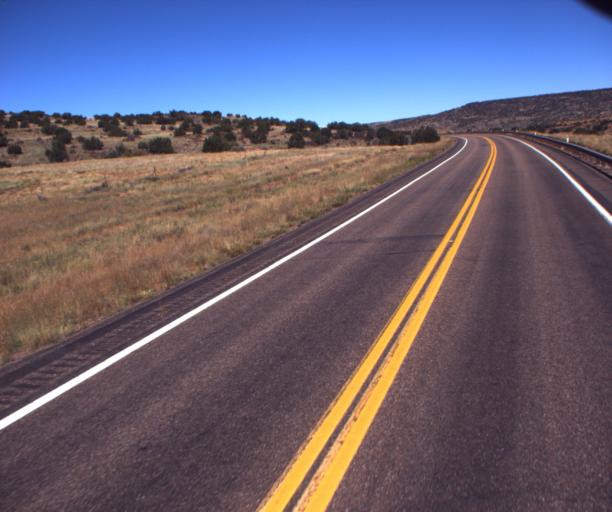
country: US
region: Arizona
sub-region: Apache County
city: Saint Johns
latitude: 34.3476
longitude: -109.3793
